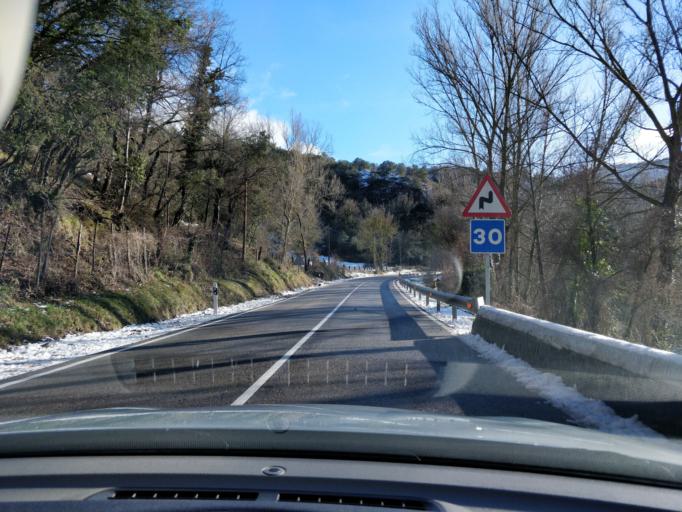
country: ES
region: Castille and Leon
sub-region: Provincia de Burgos
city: Medina de Pomar
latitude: 42.8824
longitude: -3.5982
